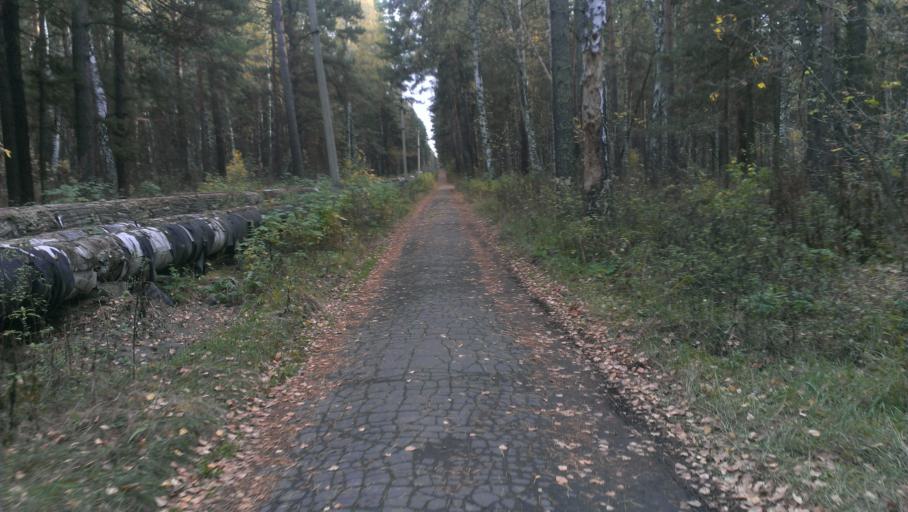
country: RU
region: Altai Krai
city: Yuzhnyy
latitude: 53.2692
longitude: 83.6817
